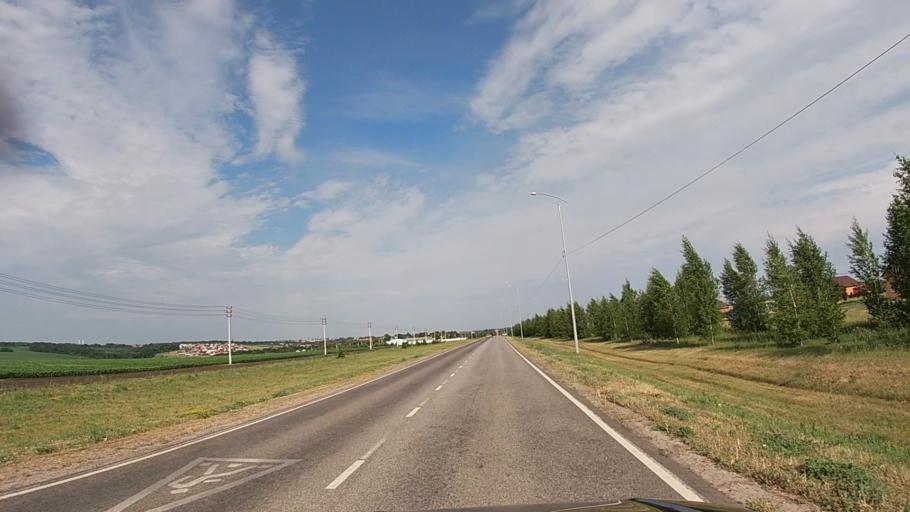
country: RU
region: Belgorod
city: Krasnaya Yaruga
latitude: 50.7972
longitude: 35.6874
